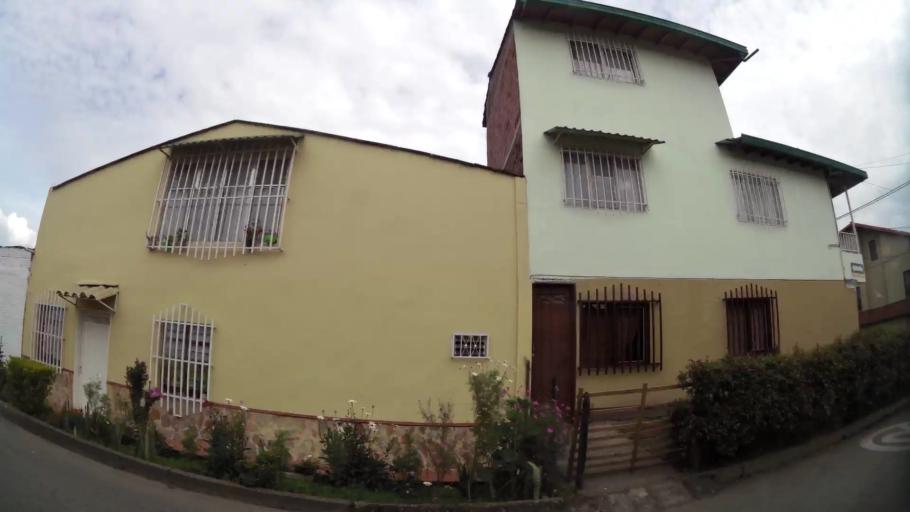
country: CO
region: Antioquia
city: Rionegro
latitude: 6.1492
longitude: -75.3883
